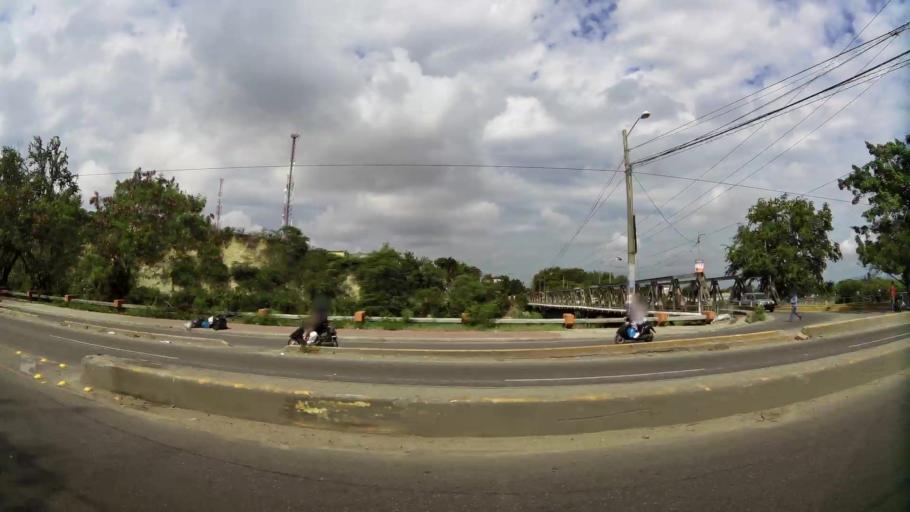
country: DO
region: Santiago
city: Santiago de los Caballeros
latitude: 19.4544
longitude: -70.7153
